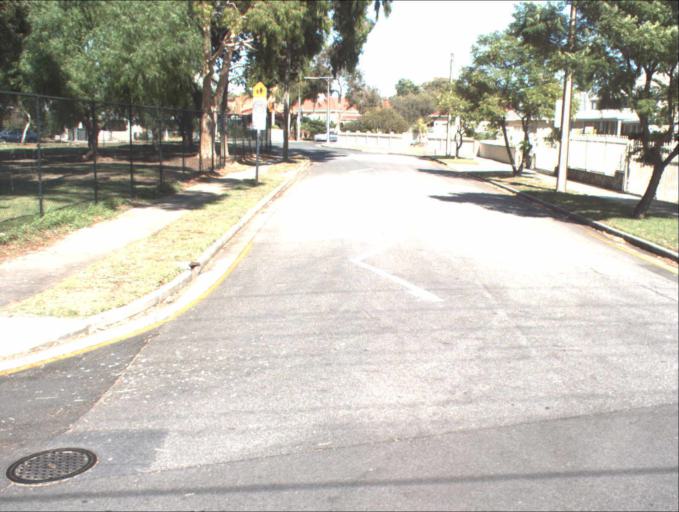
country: AU
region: South Australia
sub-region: Port Adelaide Enfield
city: Alberton
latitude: -34.8580
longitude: 138.5246
